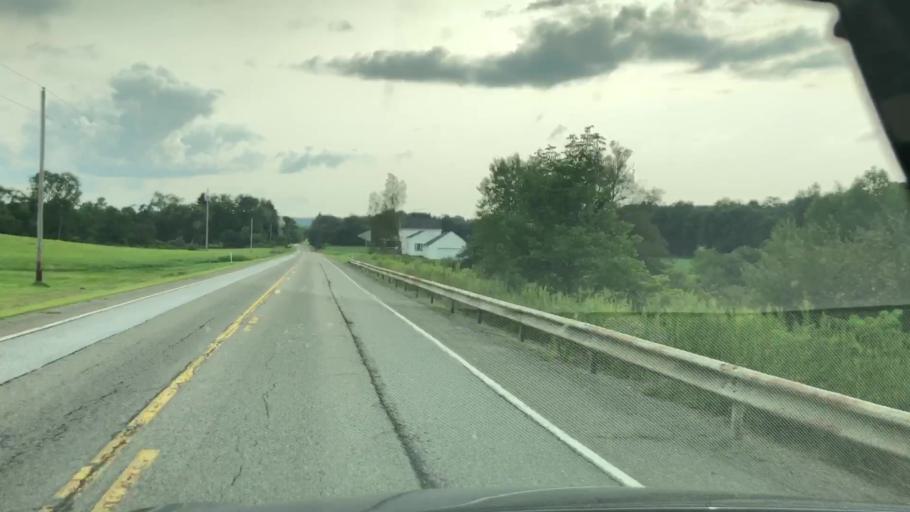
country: US
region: Pennsylvania
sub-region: Erie County
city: Union City
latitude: 41.9871
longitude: -79.8297
